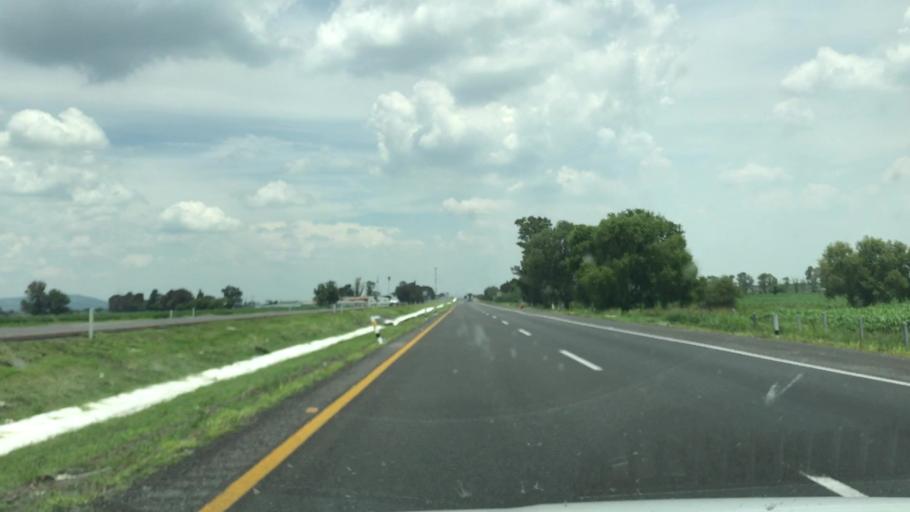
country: MX
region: Guanajuato
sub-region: Salamanca
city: San Vicente de Flores
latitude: 20.6264
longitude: -101.2436
